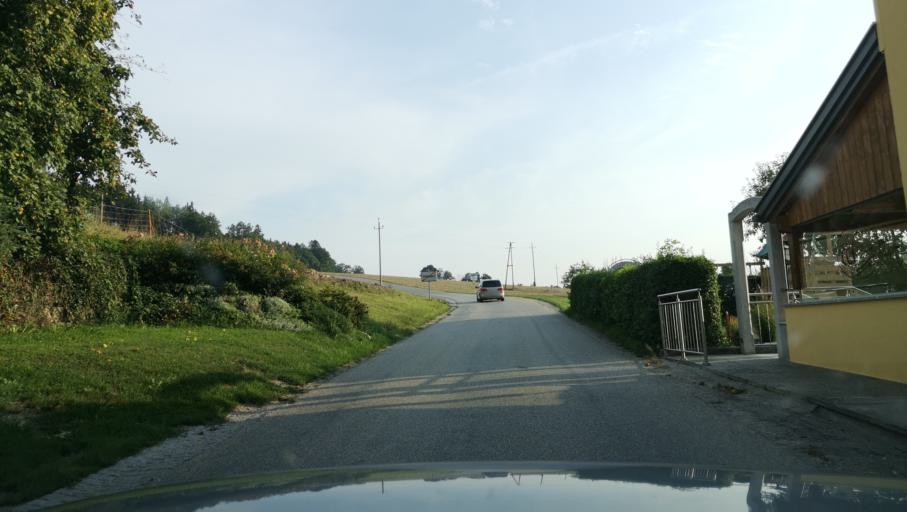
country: AT
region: Upper Austria
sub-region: Politischer Bezirk Grieskirchen
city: Grieskirchen
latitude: 48.3051
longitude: 13.7934
